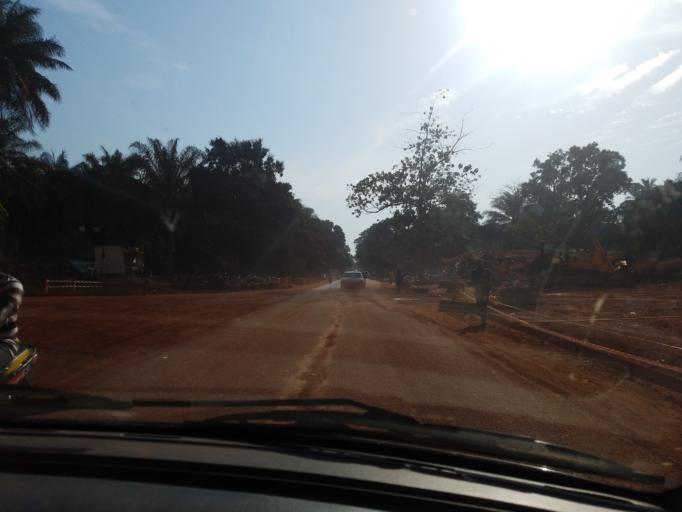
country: GN
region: Boke
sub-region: Boke Prefecture
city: Sangueya
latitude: 10.8115
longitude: -14.3843
